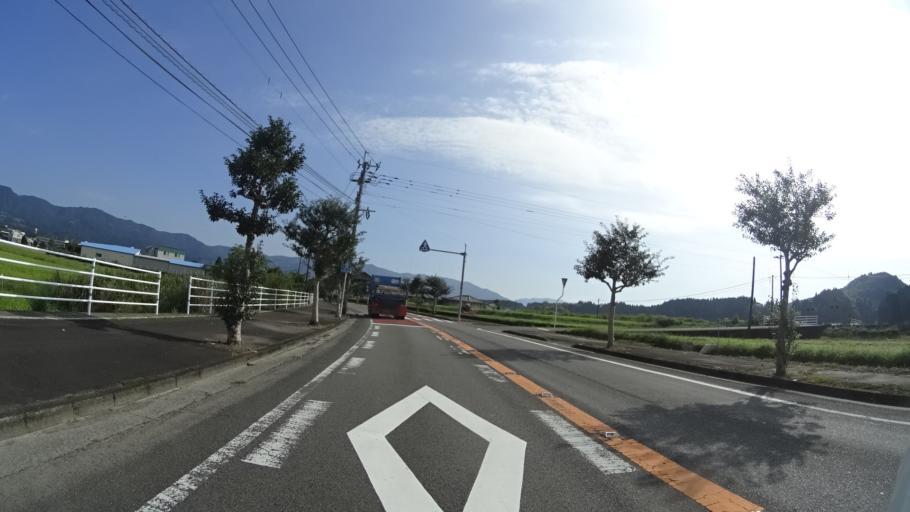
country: JP
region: Kagoshima
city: Okuchi-shinohara
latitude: 32.0415
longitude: 130.7618
